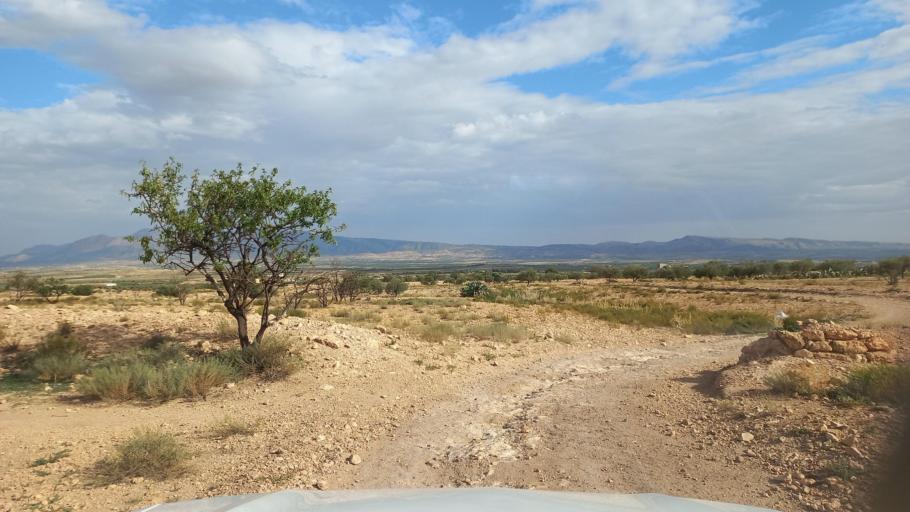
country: TN
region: Al Qasrayn
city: Sbiba
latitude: 35.4513
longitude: 9.0776
